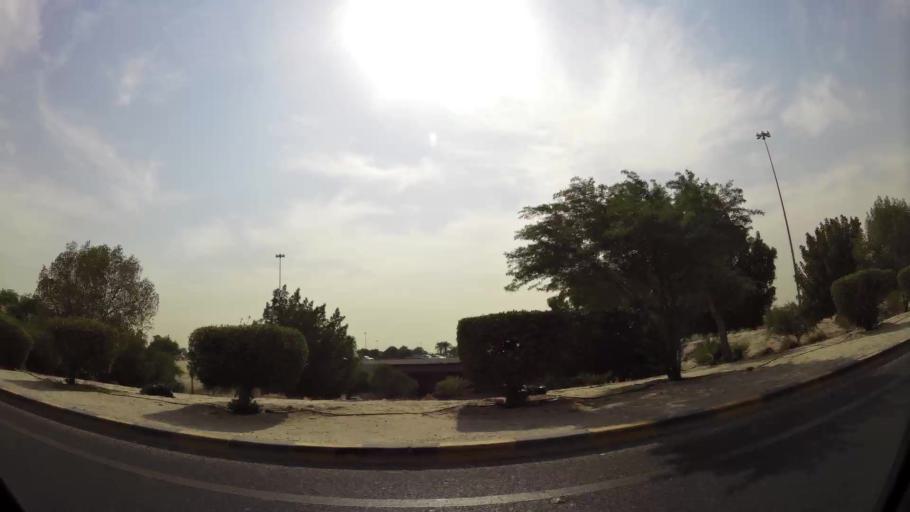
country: KW
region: Al Farwaniyah
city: Janub as Surrah
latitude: 29.2667
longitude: 47.9849
